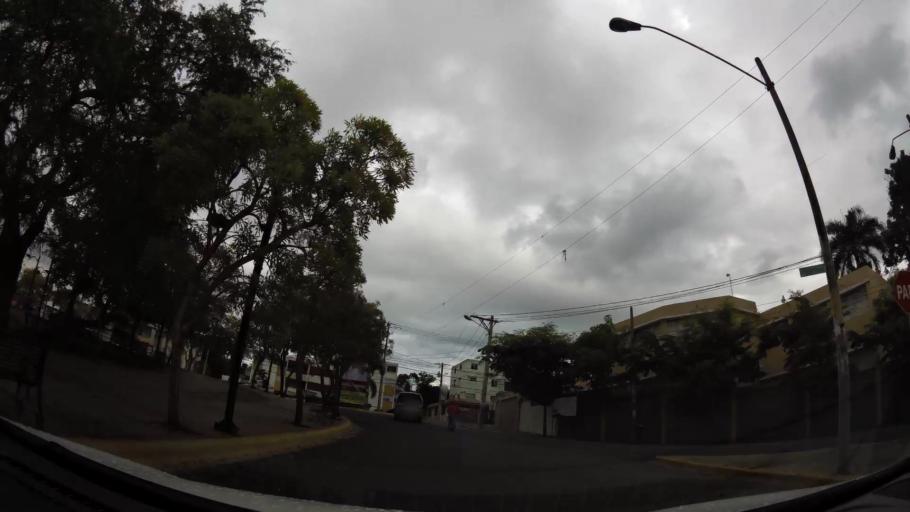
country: DO
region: Nacional
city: La Agustina
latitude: 18.4953
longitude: -69.9295
